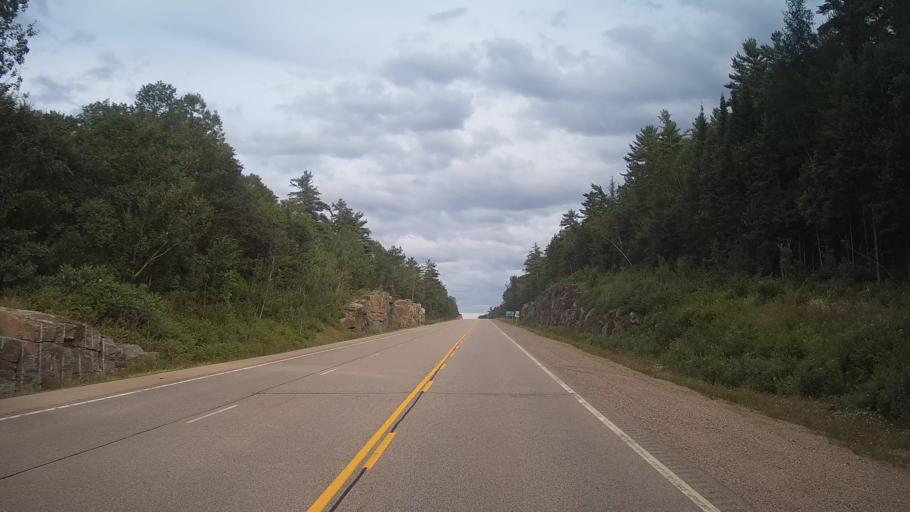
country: CA
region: Ontario
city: Mattawa
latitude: 46.2537
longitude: -78.1945
